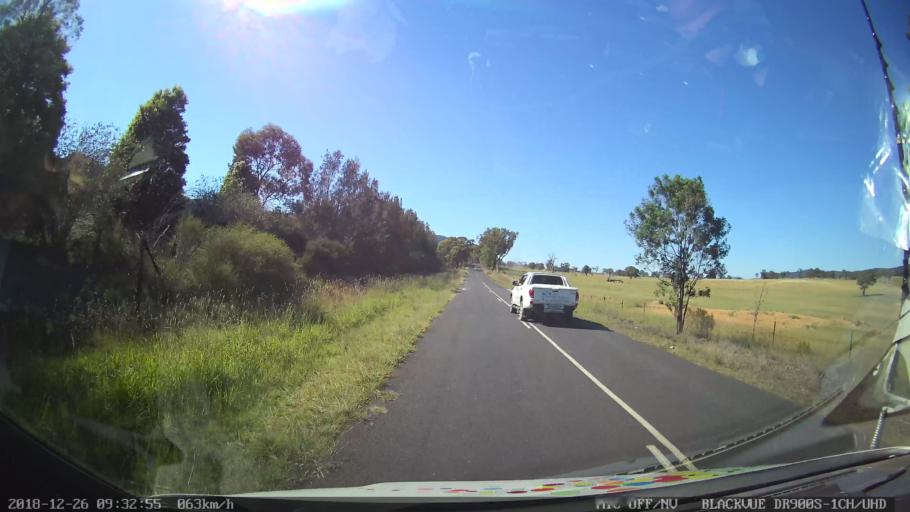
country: AU
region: New South Wales
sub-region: Mid-Western Regional
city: Kandos
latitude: -32.8895
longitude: 150.0333
